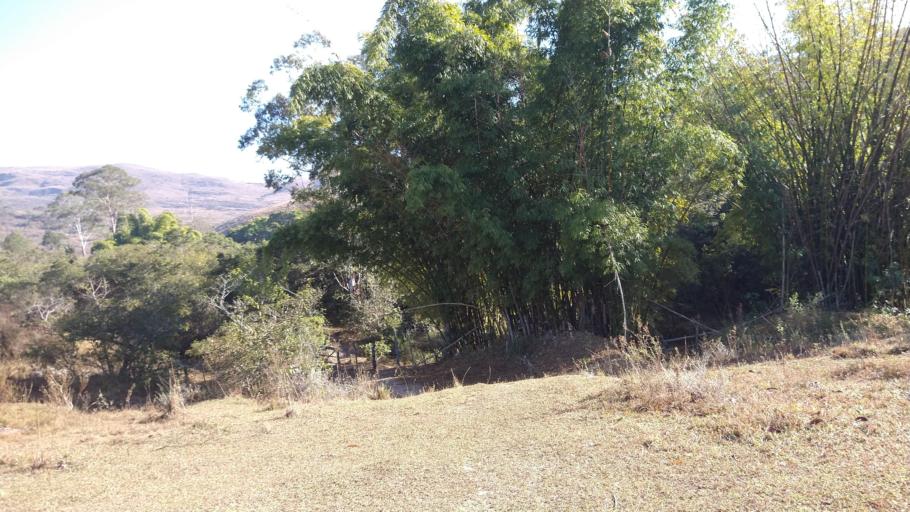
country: BR
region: Minas Gerais
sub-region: Sao Joao Del Rei
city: Sao Joao del Rei
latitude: -21.1239
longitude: -44.2738
